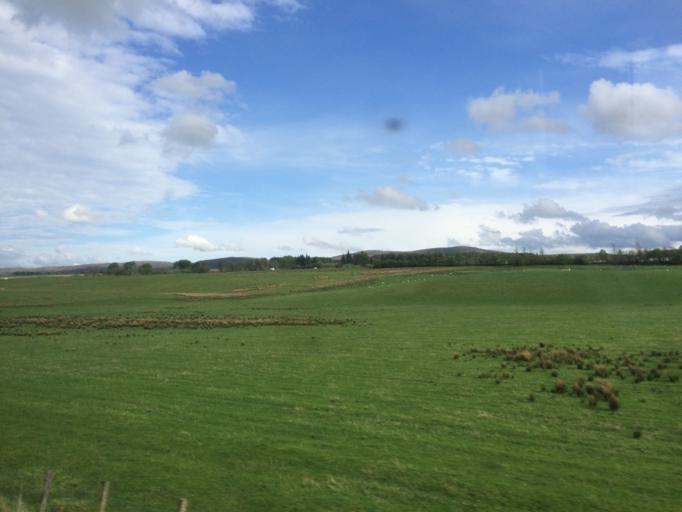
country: GB
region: Scotland
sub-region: Clackmannanshire
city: Menstrie
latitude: 56.2555
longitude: -3.8524
